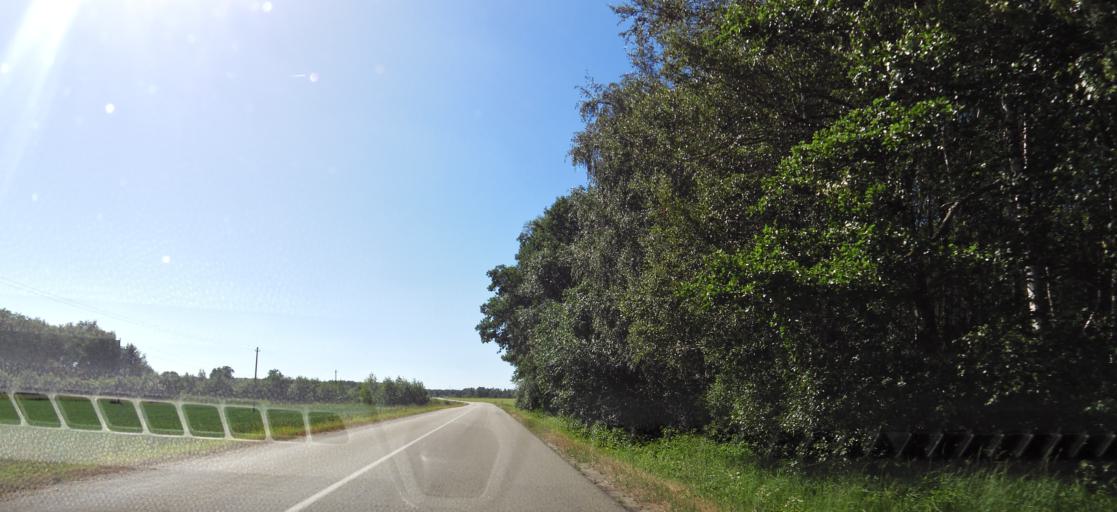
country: LT
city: Vabalninkas
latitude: 56.0025
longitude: 24.6500
